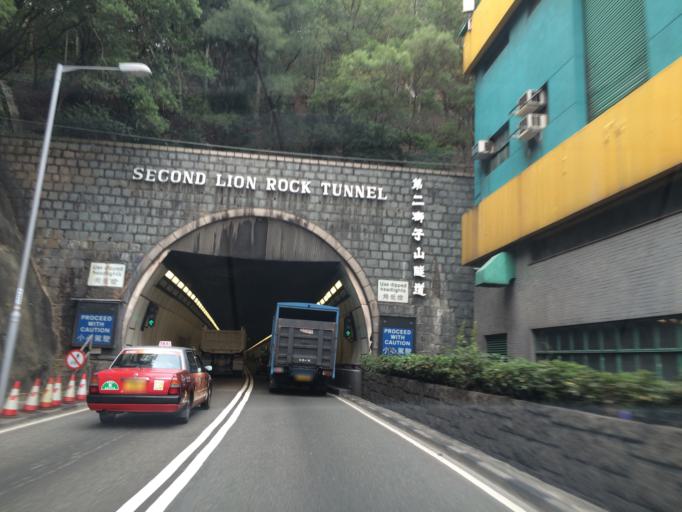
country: HK
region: Wong Tai Sin
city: Wong Tai Sin
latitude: 22.3460
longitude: 114.1812
